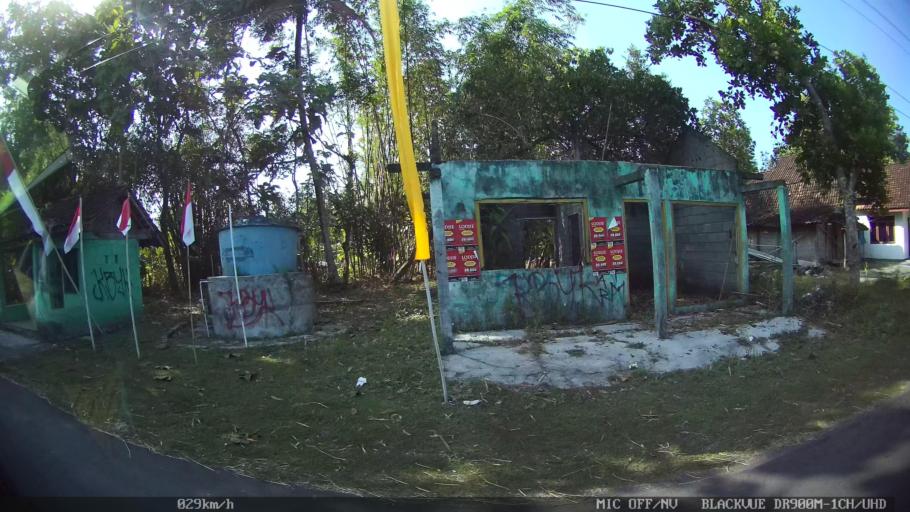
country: ID
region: Daerah Istimewa Yogyakarta
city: Kasihan
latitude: -7.8247
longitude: 110.2900
